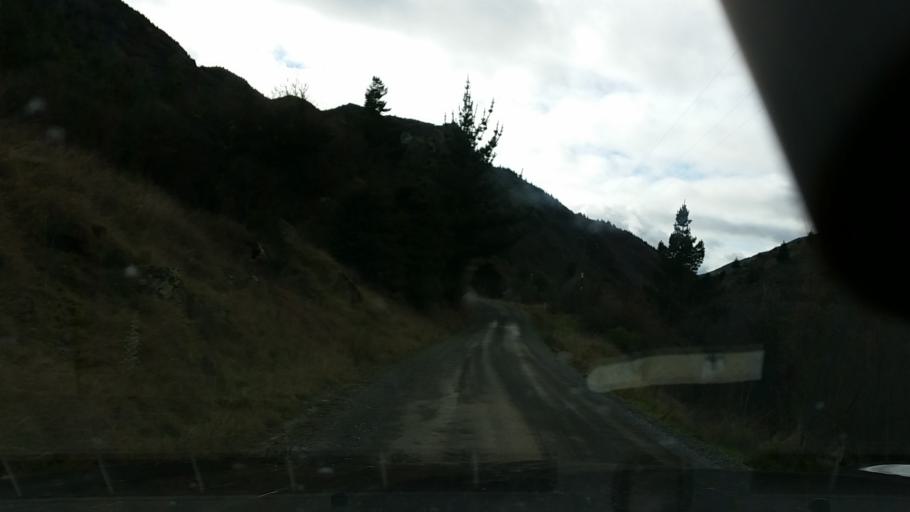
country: NZ
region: Tasman
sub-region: Tasman District
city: Richmond
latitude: -41.7200
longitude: 173.4721
